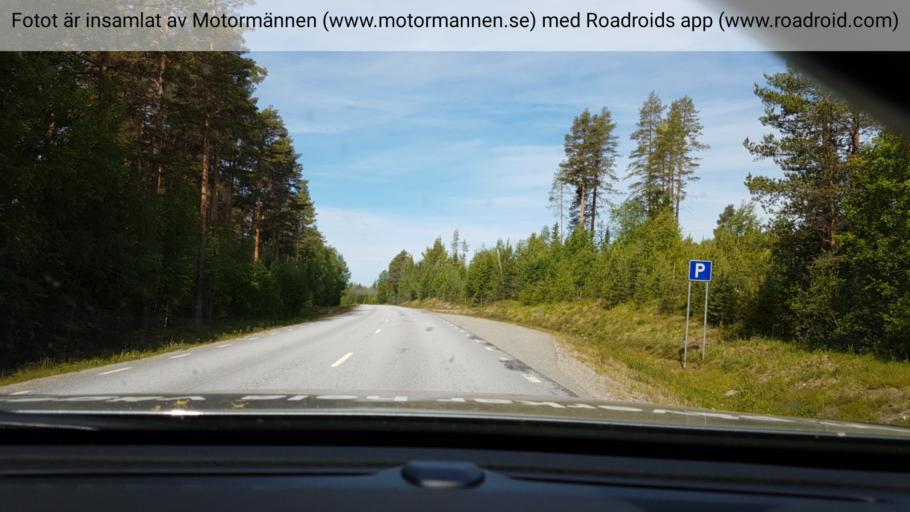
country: SE
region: Vaesterbotten
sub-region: Asele Kommun
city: Asele
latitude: 64.1887
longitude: 17.1635
